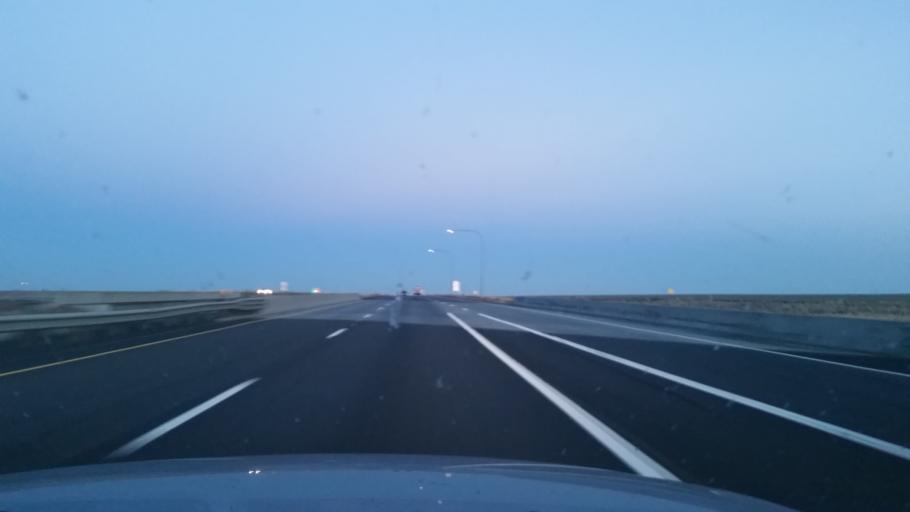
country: US
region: Washington
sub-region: Adams County
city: Ritzville
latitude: 47.1112
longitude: -118.3901
